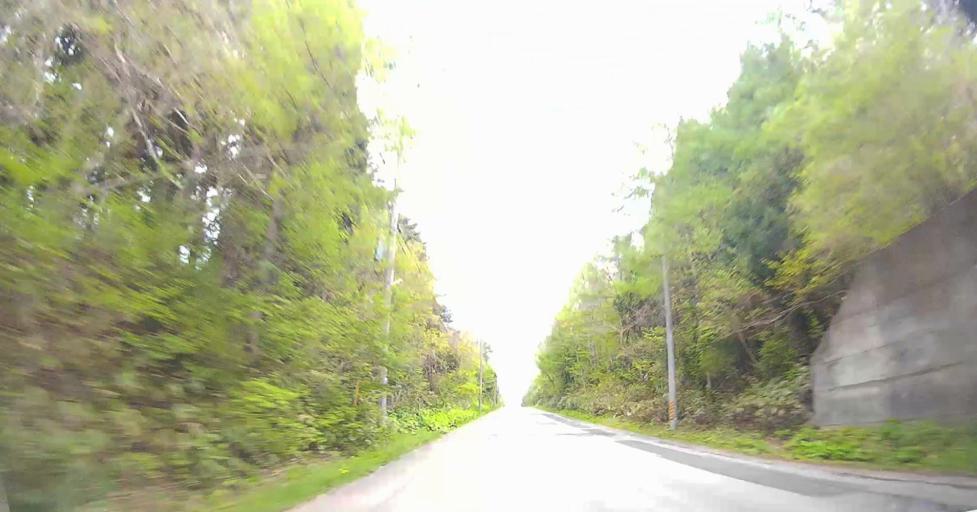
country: JP
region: Aomori
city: Shimokizukuri
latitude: 41.1786
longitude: 140.4709
